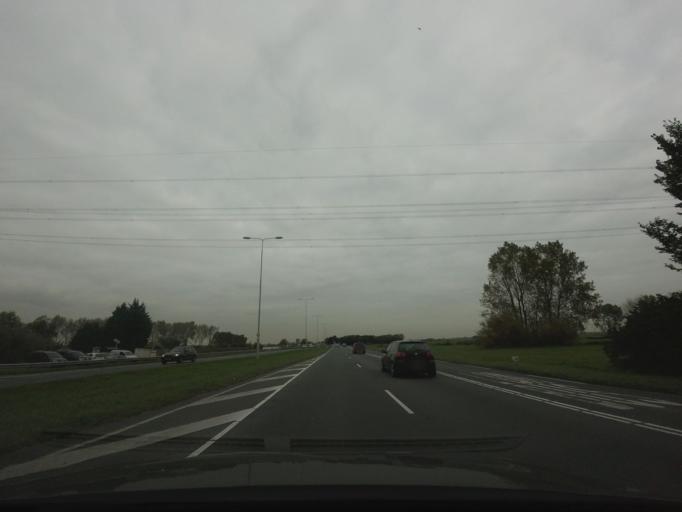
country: NL
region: North Holland
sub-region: Gemeente Landsmeer
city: Landsmeer
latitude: 52.4120
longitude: 4.9435
